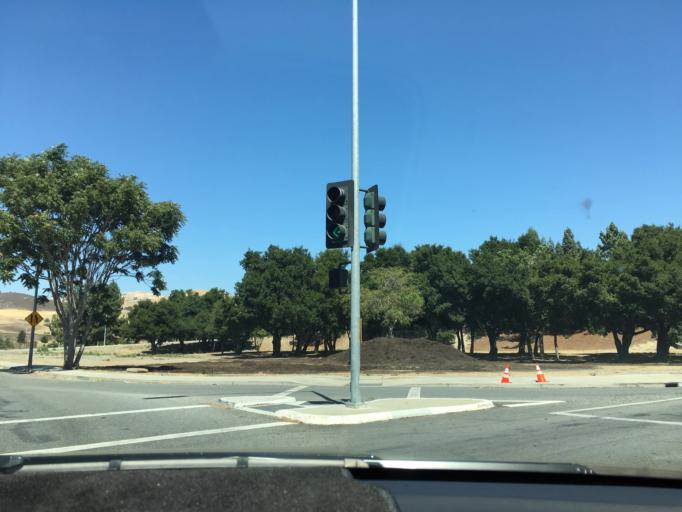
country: US
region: California
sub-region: Santa Clara County
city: Seven Trees
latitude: 37.2388
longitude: -121.7744
